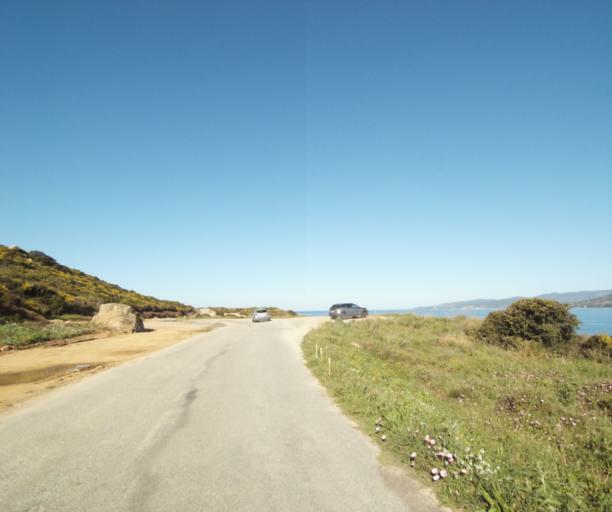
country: FR
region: Corsica
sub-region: Departement de la Corse-du-Sud
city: Propriano
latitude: 41.6711
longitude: 8.8890
